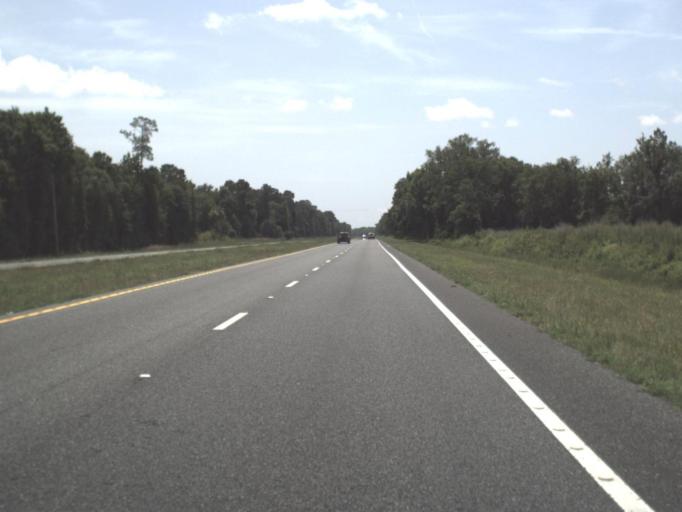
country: US
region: Florida
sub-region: Taylor County
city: Perry
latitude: 29.9781
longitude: -83.4875
